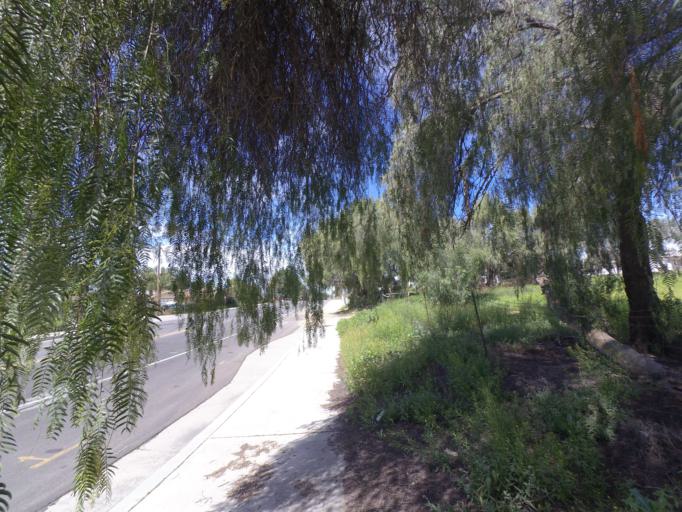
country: US
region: California
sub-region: Riverside County
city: March Air Force Base
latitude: 33.9207
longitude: -117.2740
